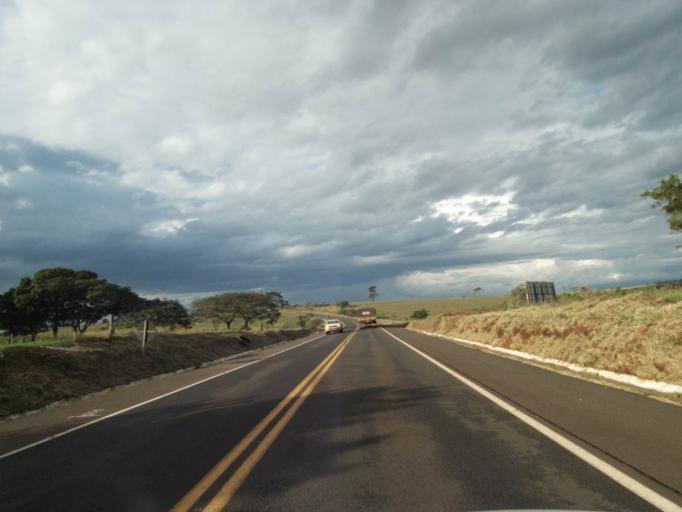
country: PY
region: Canindeyu
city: Salto del Guaira
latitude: -24.0835
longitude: -54.0711
